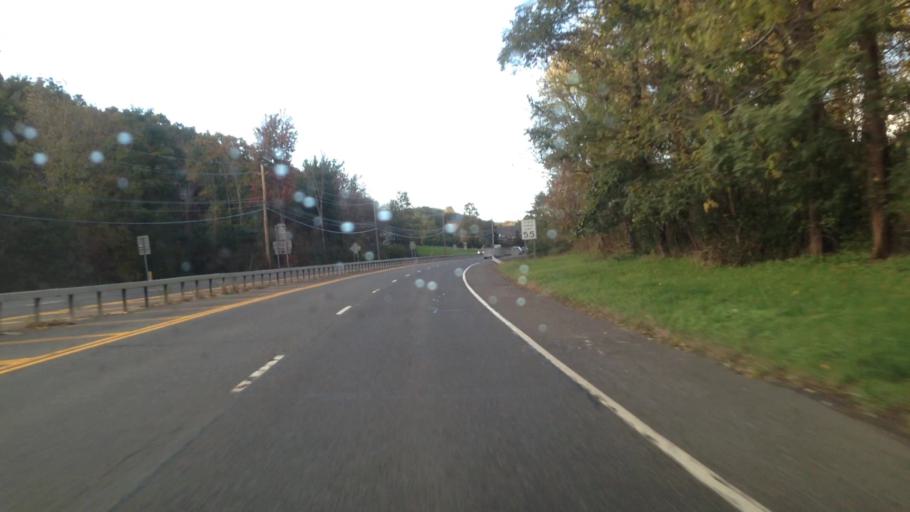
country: US
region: New York
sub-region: Ulster County
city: Highland
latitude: 41.7434
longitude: -73.9647
